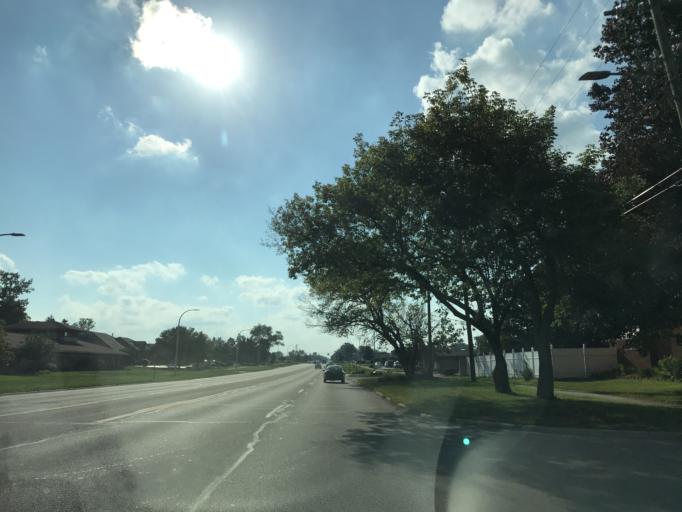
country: US
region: Michigan
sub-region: Wayne County
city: Livonia
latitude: 42.3968
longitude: -83.3984
